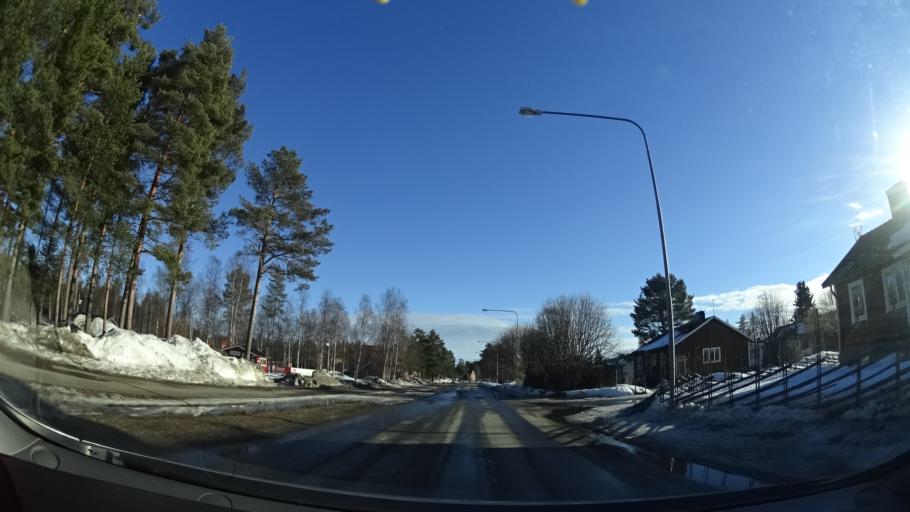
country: SE
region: Vaesterbotten
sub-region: Skelleftea Kommun
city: Byske
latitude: 64.9545
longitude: 21.2134
